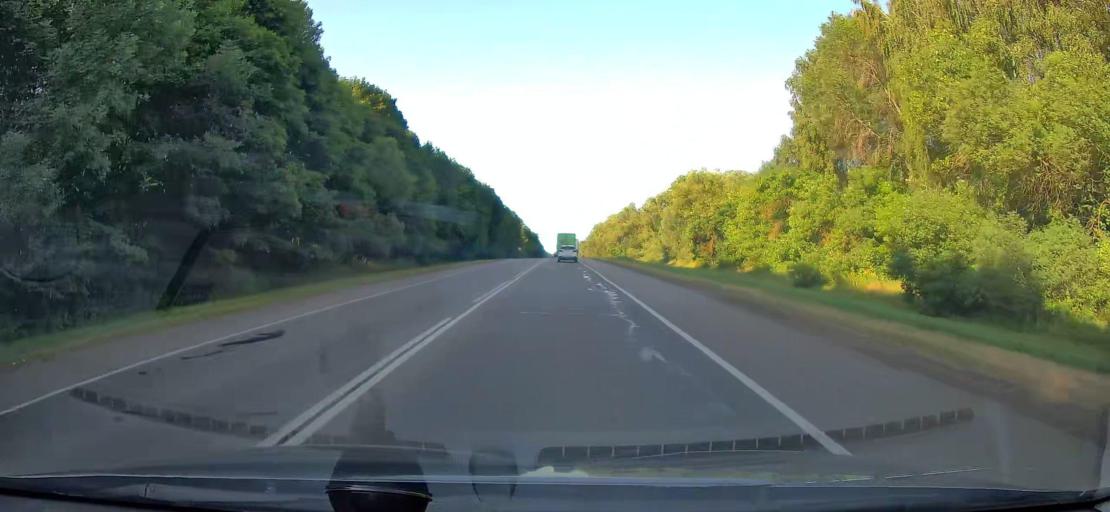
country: RU
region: Tula
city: Plavsk
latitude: 53.5809
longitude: 37.1445
